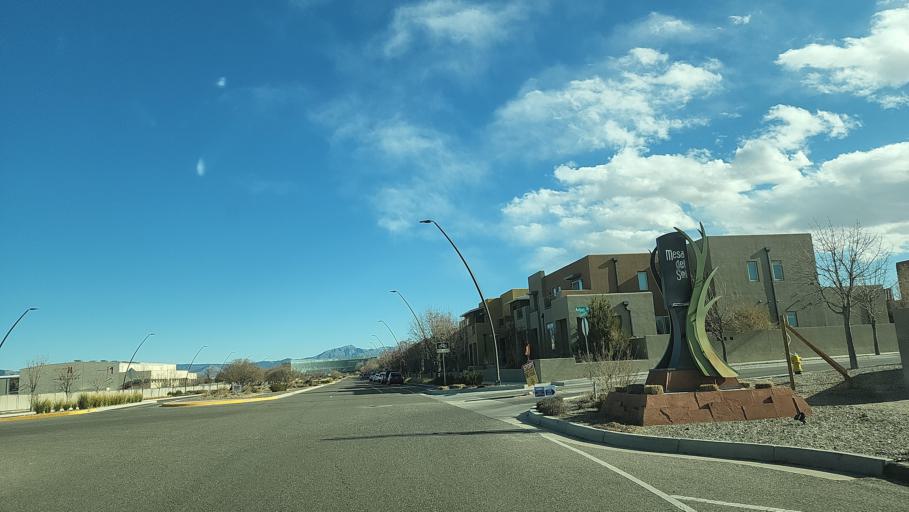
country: US
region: New Mexico
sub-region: Bernalillo County
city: South Valley
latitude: 34.9907
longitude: -106.6182
